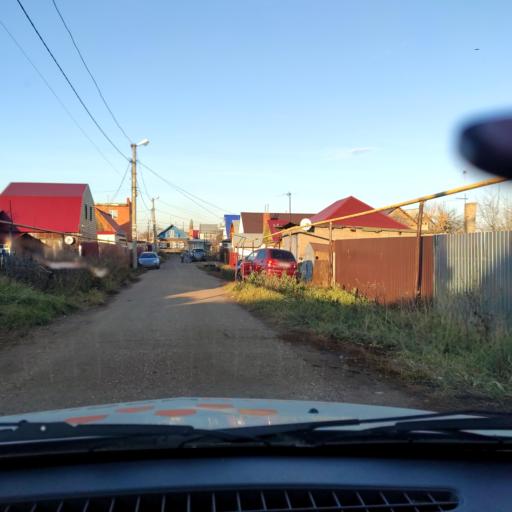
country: RU
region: Bashkortostan
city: Ufa
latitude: 54.7742
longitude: 56.0526
